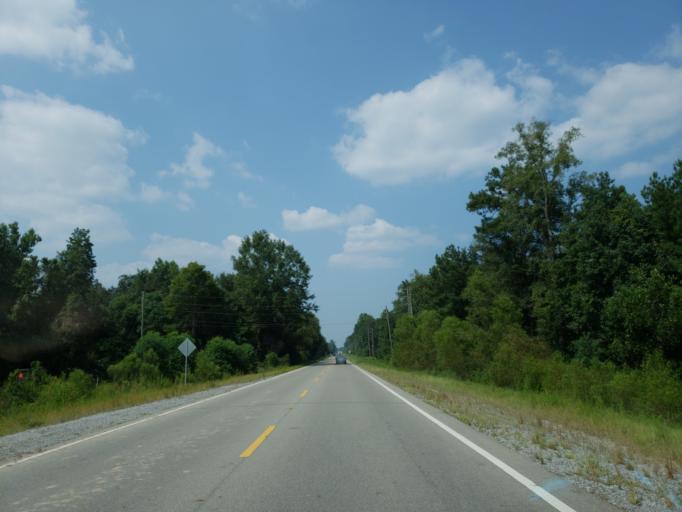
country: US
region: Mississippi
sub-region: Forrest County
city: Glendale
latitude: 31.4670
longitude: -89.2838
